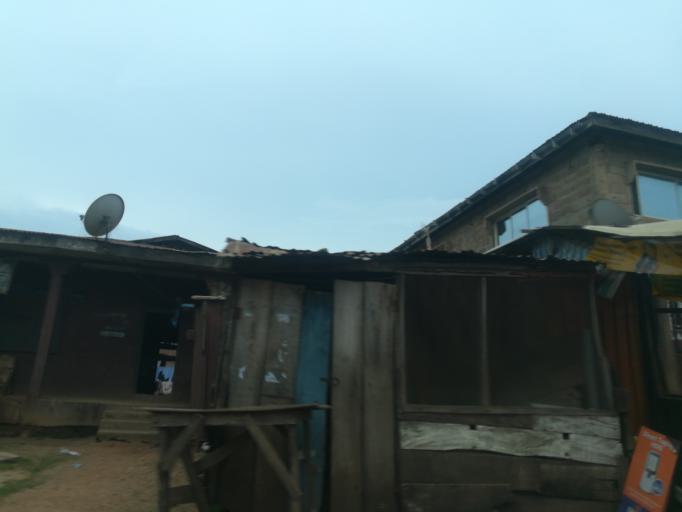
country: NG
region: Oyo
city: Ibadan
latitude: 7.4421
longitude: 3.9102
